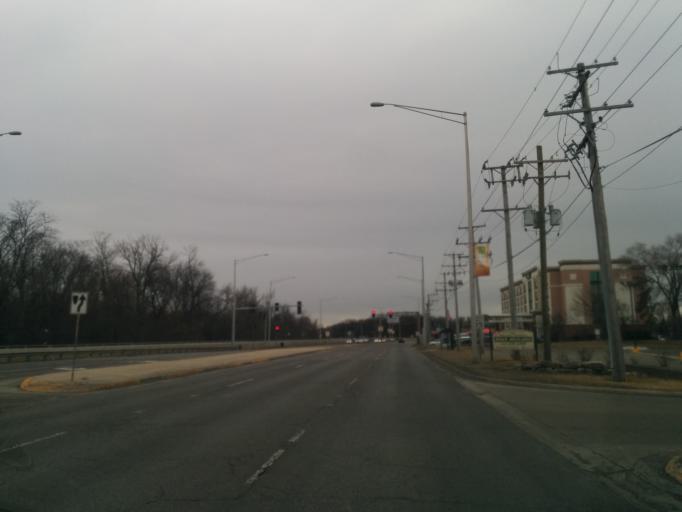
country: US
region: Illinois
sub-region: Cook County
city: Prospect Heights
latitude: 42.1077
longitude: -87.8895
